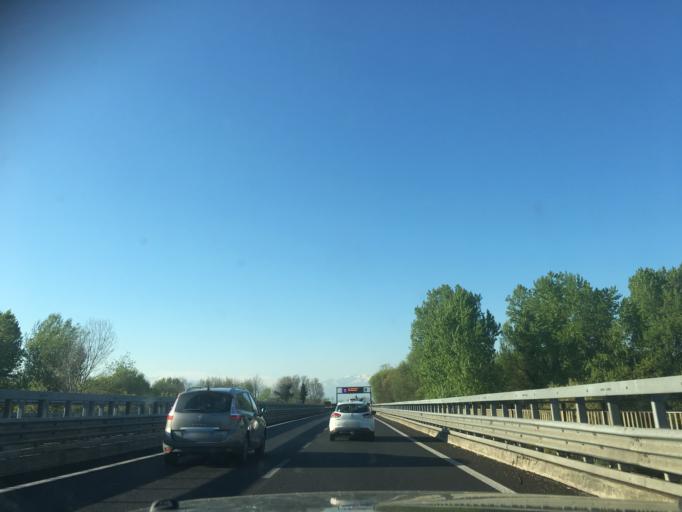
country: IT
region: Piedmont
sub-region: Provincia di Torino
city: Turin
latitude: 45.1136
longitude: 7.6956
